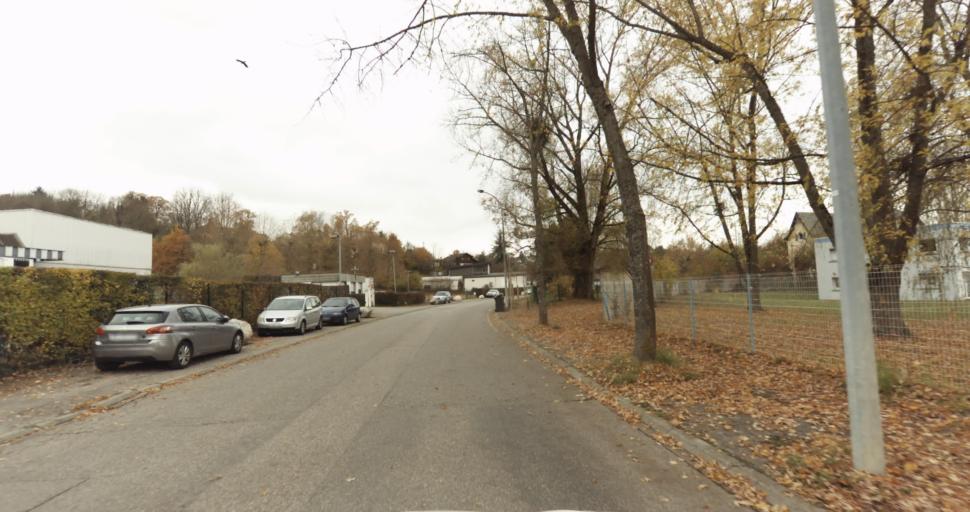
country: FR
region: Rhone-Alpes
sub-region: Departement de la Haute-Savoie
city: Annecy
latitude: 45.8817
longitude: 6.1172
